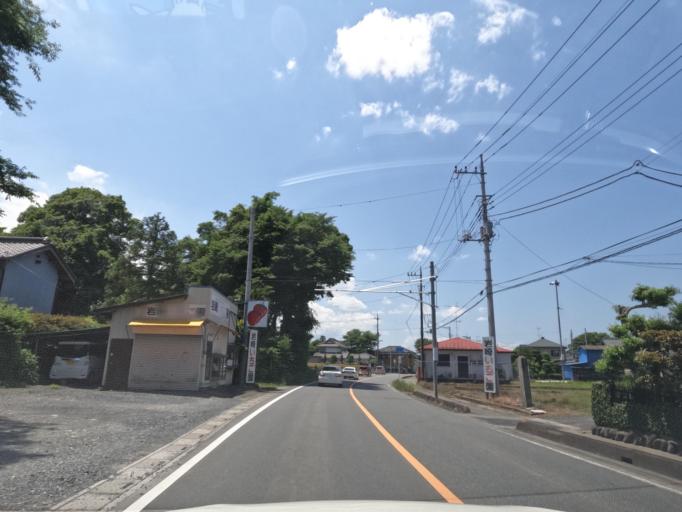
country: JP
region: Saitama
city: Konosu
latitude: 36.0220
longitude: 139.4726
